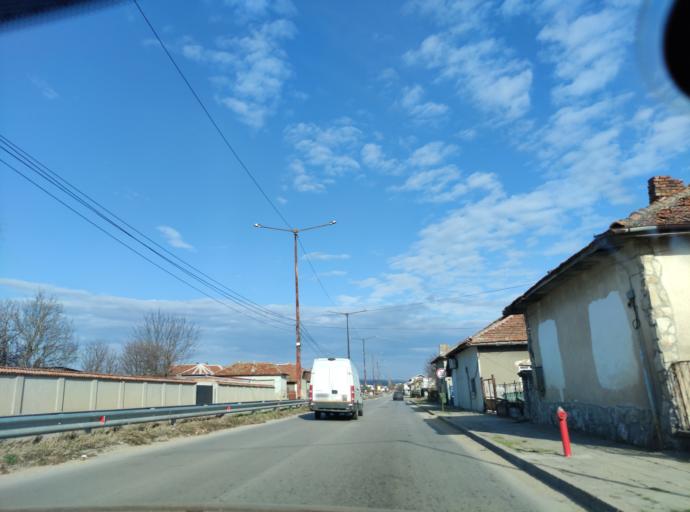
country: BG
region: Pleven
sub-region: Obshtina Dolna Mitropoliya
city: Dolna Mitropoliya
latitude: 43.4300
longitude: 24.5197
